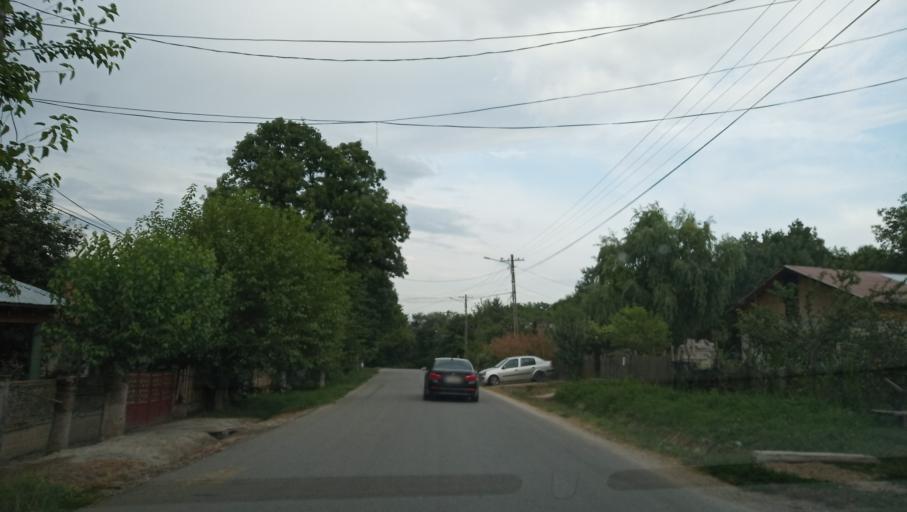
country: RO
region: Giurgiu
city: Iepuresti
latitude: 44.2566
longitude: 25.8890
